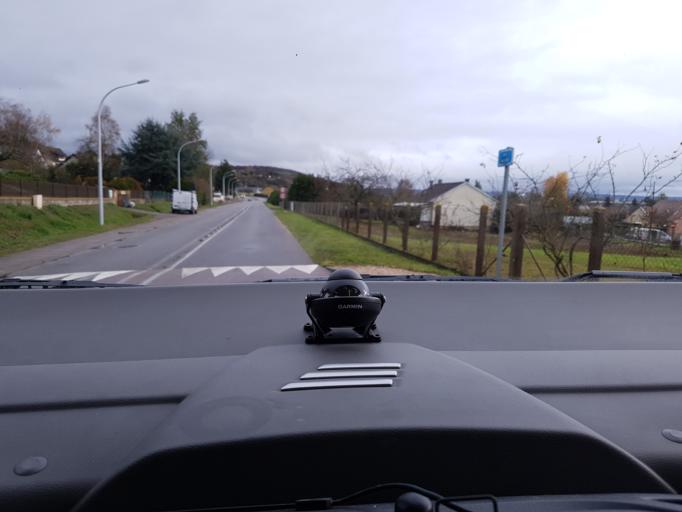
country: FR
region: Haute-Normandie
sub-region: Departement de l'Eure
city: Igoville
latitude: 49.3203
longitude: 1.1395
